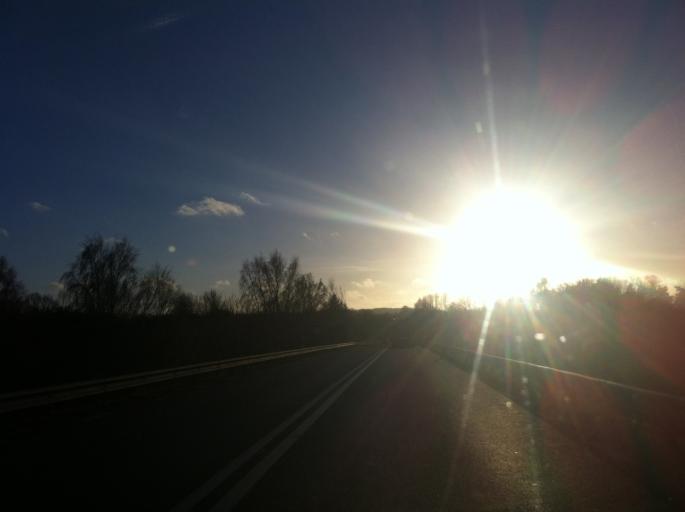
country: SE
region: Skane
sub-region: Hassleholms Kommun
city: Vinslov
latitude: 56.1853
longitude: 13.8846
